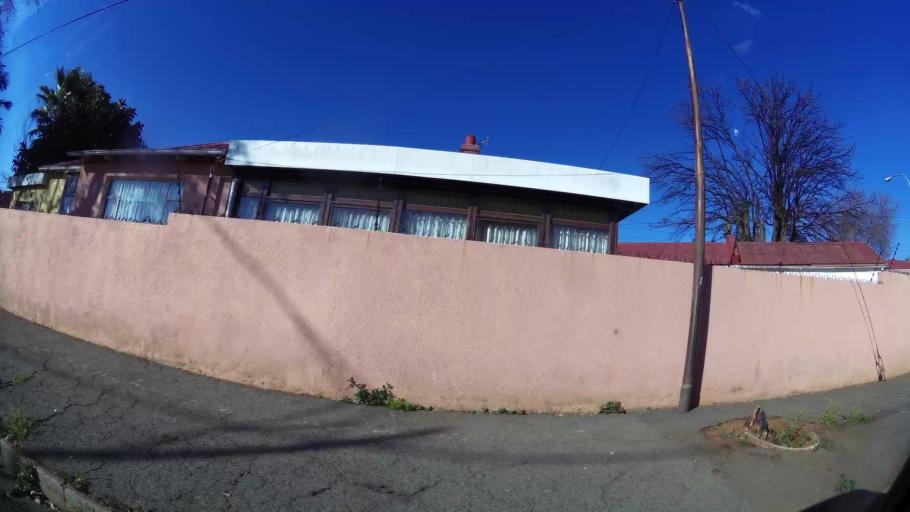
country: ZA
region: Gauteng
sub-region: City of Johannesburg Metropolitan Municipality
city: Johannesburg
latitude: -26.1915
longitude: 28.0915
